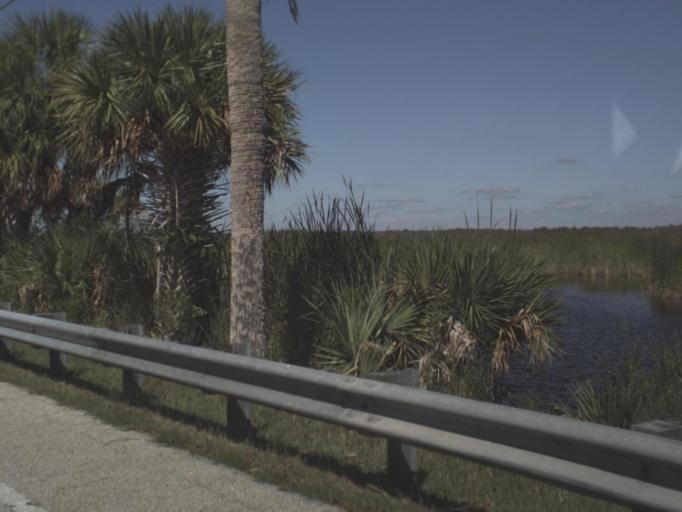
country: US
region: Florida
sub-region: Collier County
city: Marco
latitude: 25.9209
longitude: -81.4059
